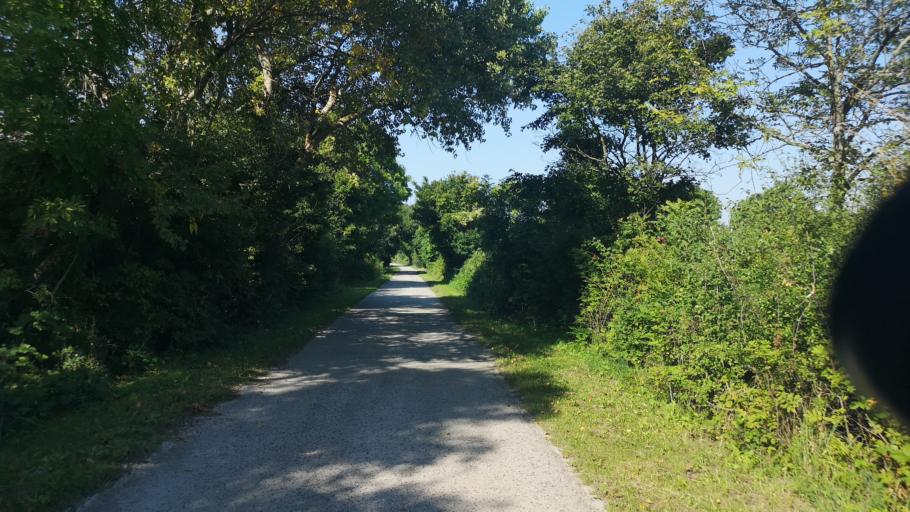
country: SK
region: Trnavsky
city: Smolenice
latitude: 48.5737
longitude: 17.4088
